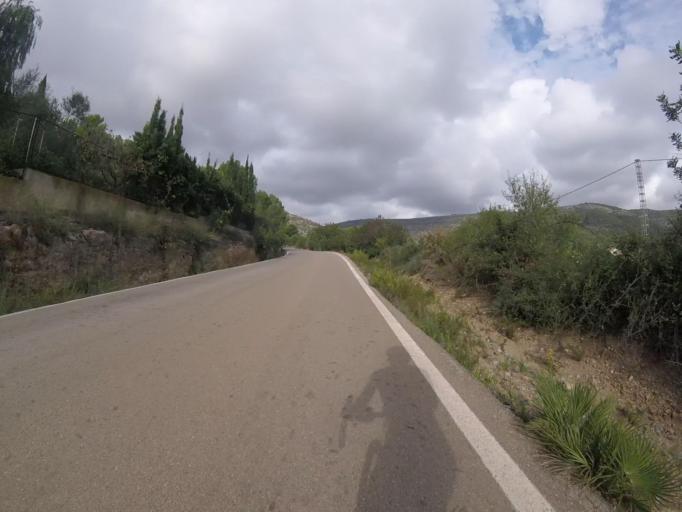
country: ES
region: Valencia
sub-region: Provincia de Castello
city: Orpesa/Oropesa del Mar
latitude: 40.1400
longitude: 0.1174
